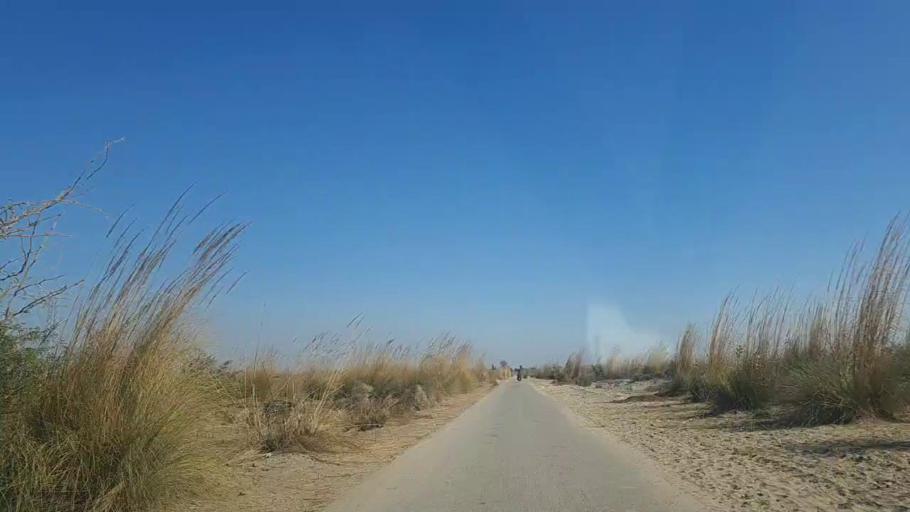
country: PK
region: Sindh
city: Khadro
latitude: 26.2094
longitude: 68.8311
